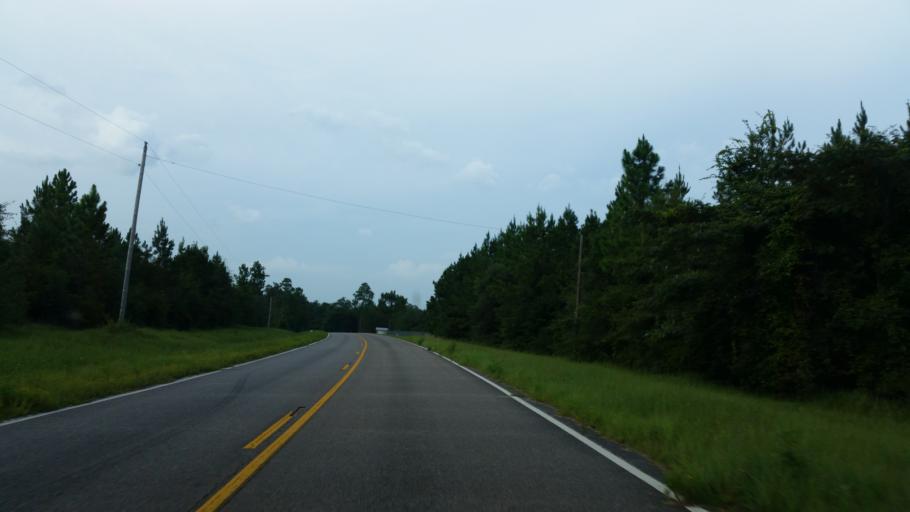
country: US
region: Florida
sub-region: Escambia County
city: Molino
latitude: 30.7844
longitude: -87.5243
